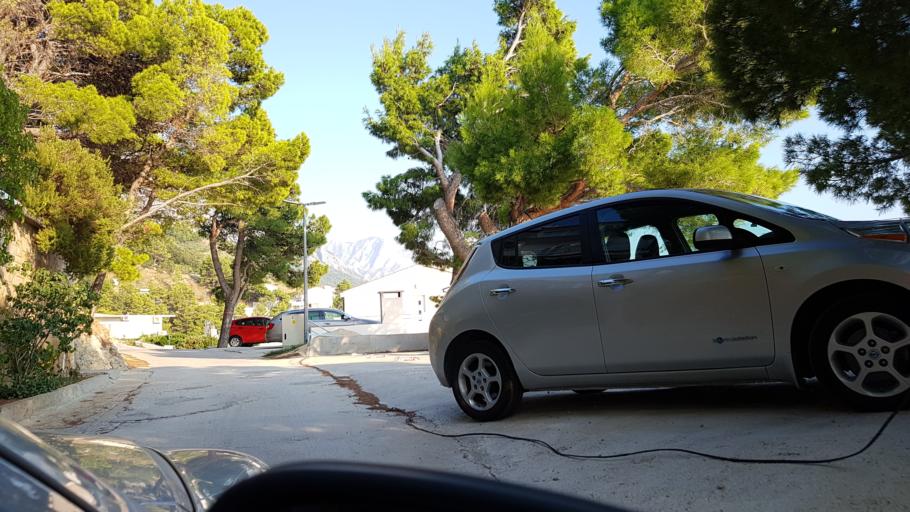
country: HR
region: Splitsko-Dalmatinska
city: Donja Brela
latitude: 43.3872
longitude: 16.9005
